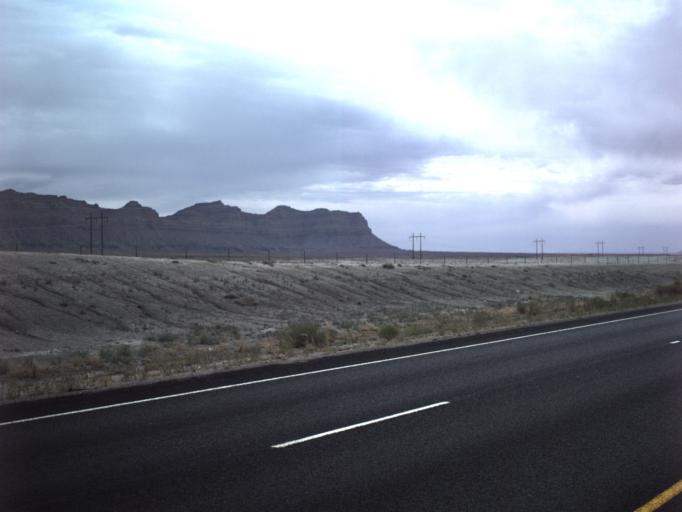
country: US
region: Utah
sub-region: Carbon County
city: East Carbon City
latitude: 39.1536
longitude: -110.3379
